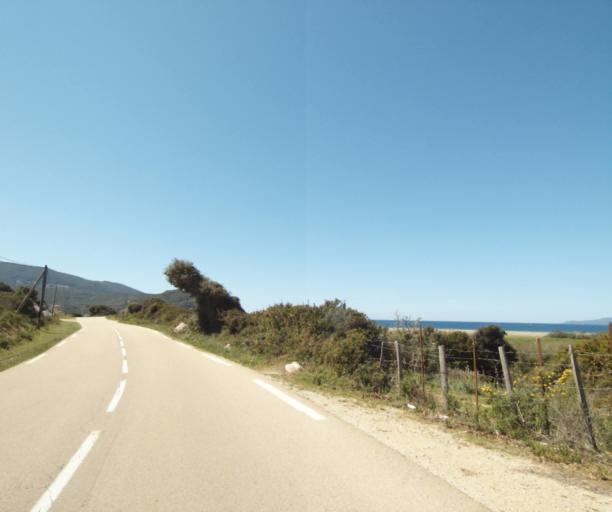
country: FR
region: Corsica
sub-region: Departement de la Corse-du-Sud
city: Propriano
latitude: 41.6525
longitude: 8.8821
